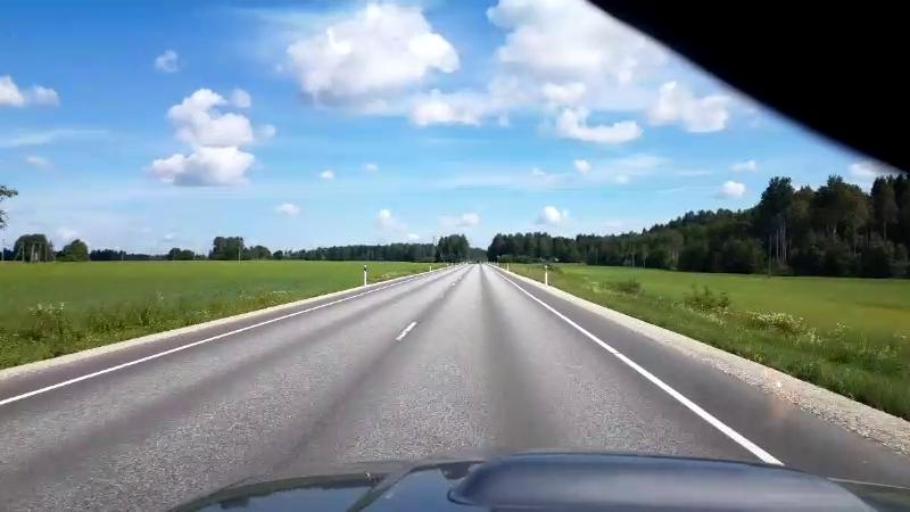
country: EE
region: Jaervamaa
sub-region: Paide linn
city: Paide
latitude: 58.9923
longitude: 25.6734
